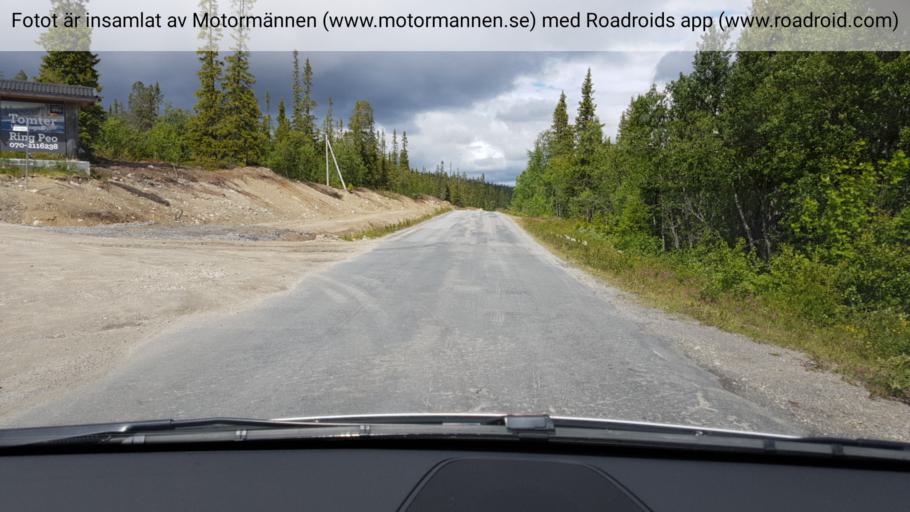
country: SE
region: Jaemtland
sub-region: Bergs Kommun
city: Hoverberg
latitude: 62.4955
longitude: 14.1131
